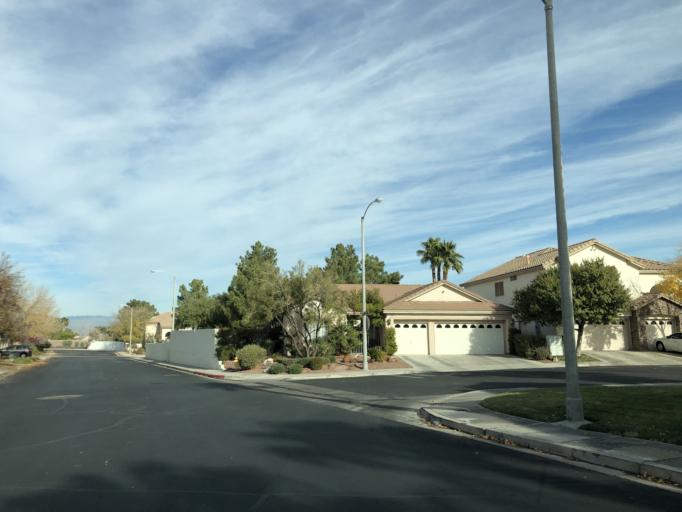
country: US
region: Nevada
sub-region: Clark County
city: Whitney
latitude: 36.0188
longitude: -115.0716
